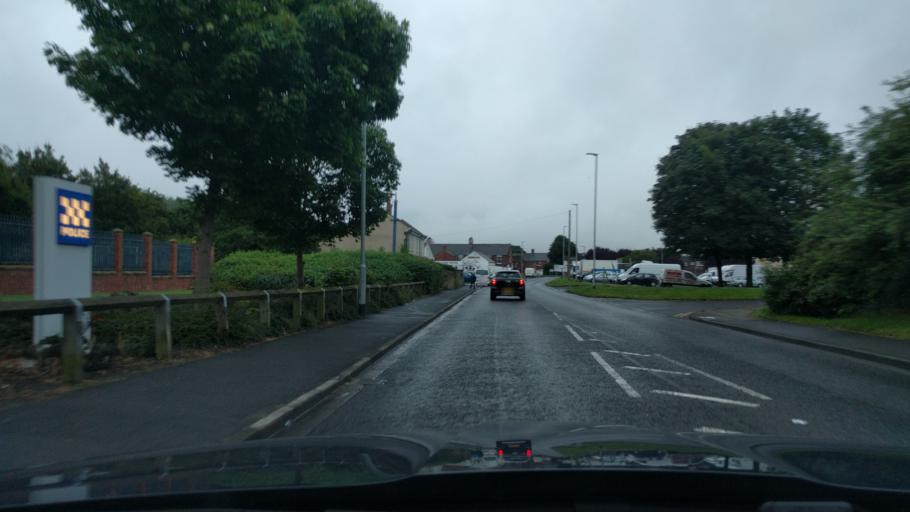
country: GB
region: England
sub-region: Northumberland
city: Bedlington
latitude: 55.1328
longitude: -1.5934
